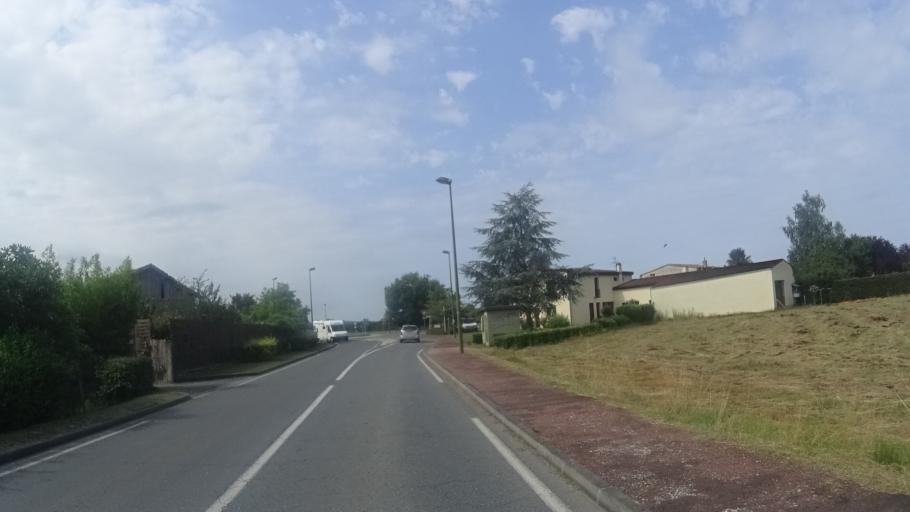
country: FR
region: Aquitaine
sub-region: Departement de la Dordogne
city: Mussidan
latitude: 45.0550
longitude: 0.3635
